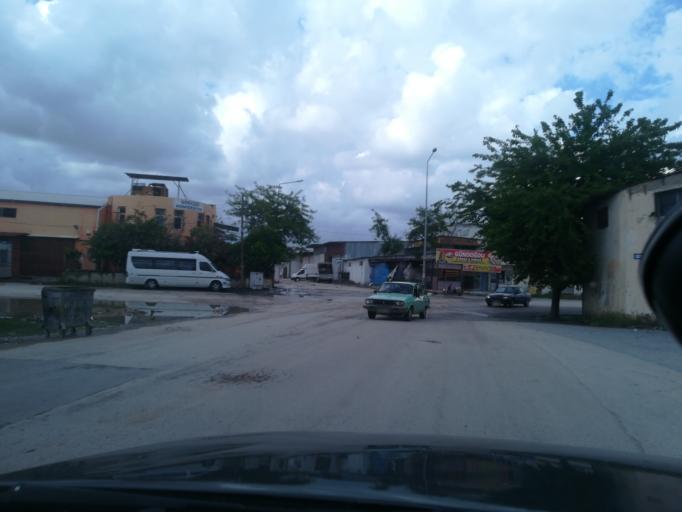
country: TR
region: Adana
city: Yuregir
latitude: 36.9773
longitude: 35.3916
